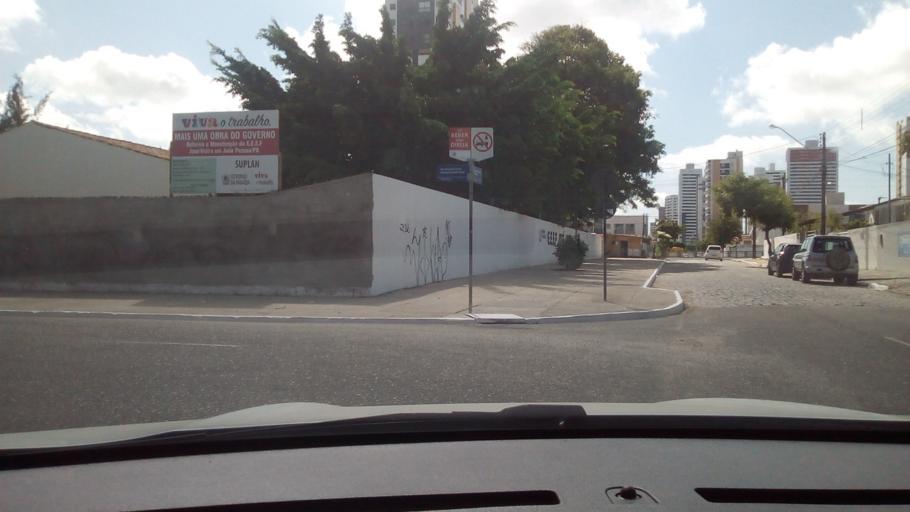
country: BR
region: Paraiba
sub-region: Joao Pessoa
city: Joao Pessoa
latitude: -7.1217
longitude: -34.8441
